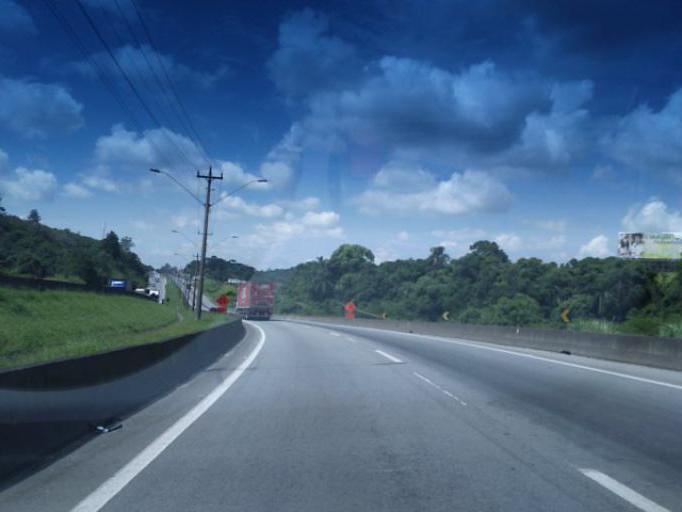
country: BR
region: Sao Paulo
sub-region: Itapecerica Da Serra
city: Itapecerica da Serra
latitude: -23.7241
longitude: -46.8926
